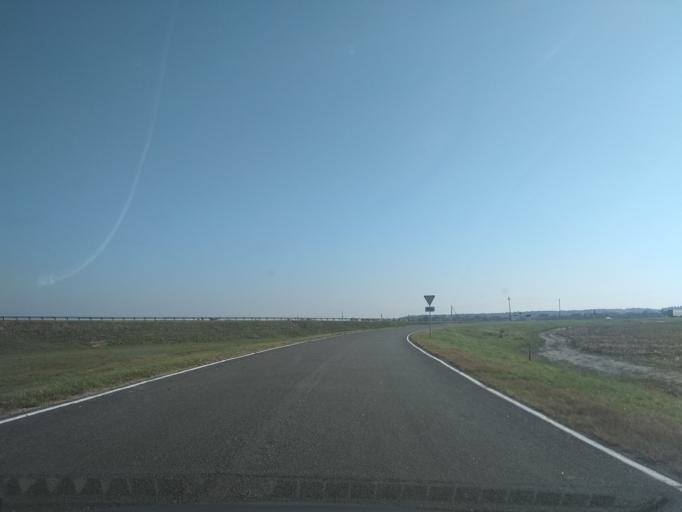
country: BY
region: Brest
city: Ivatsevichy
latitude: 52.6973
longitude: 25.3619
